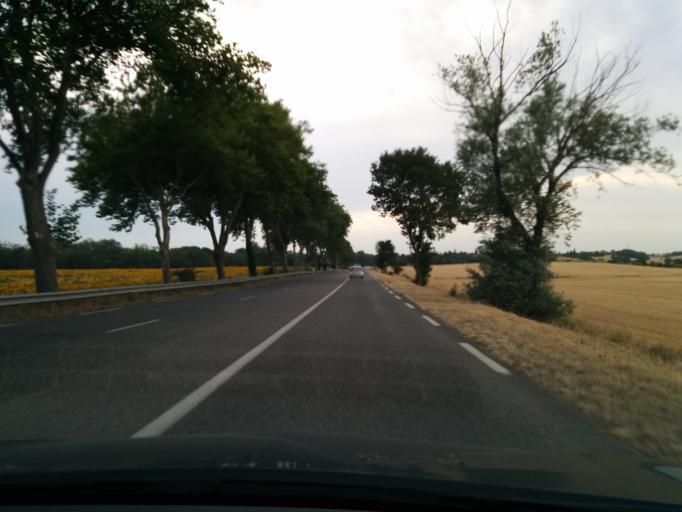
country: FR
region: Languedoc-Roussillon
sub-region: Departement de l'Aude
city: Saint-Martin-Lalande
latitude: 43.2961
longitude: 2.0064
